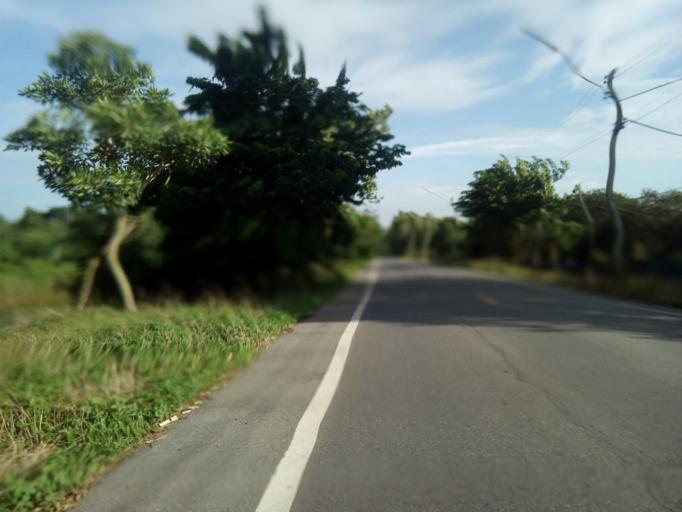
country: TH
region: Pathum Thani
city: Nong Suea
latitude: 14.1181
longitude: 100.8461
